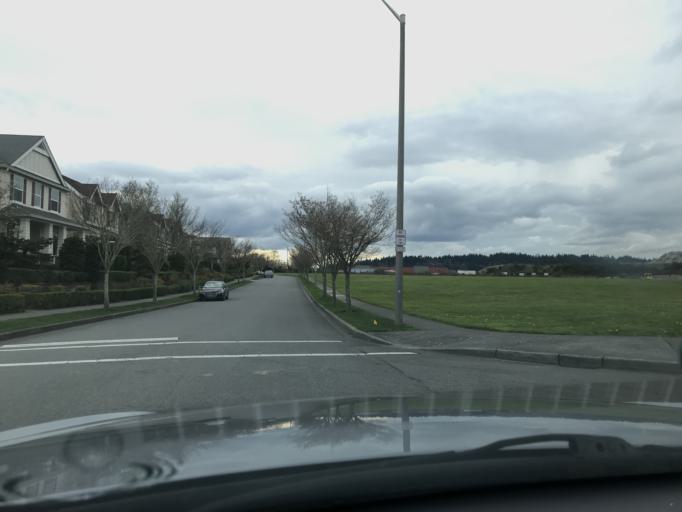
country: US
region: Washington
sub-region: King County
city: Sammamish
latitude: 47.6657
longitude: -122.0843
